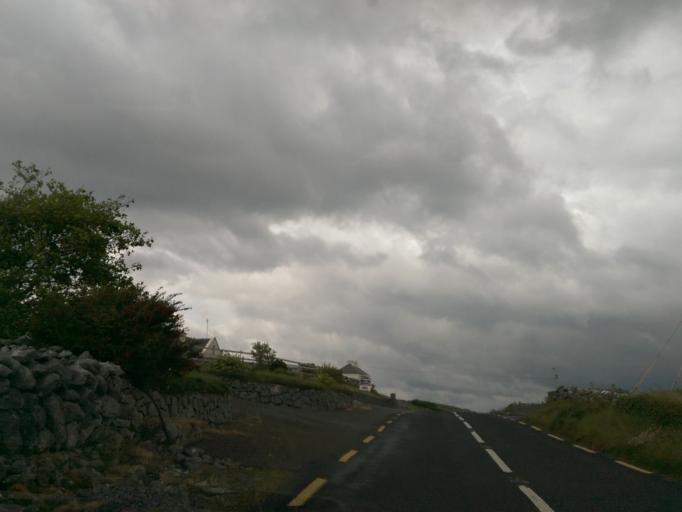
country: IE
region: Connaught
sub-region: County Galway
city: Gaillimh
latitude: 53.1505
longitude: -9.0630
